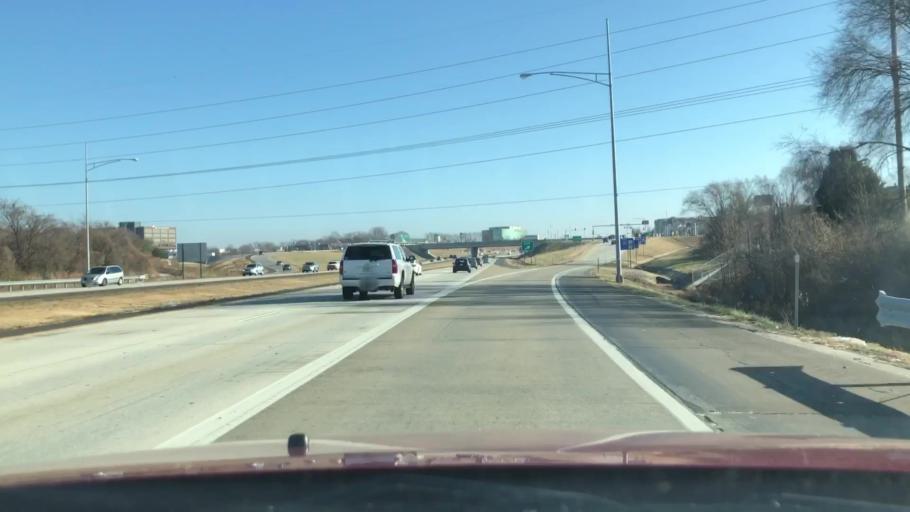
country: US
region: Missouri
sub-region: Greene County
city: Springfield
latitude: 37.1402
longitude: -93.2832
